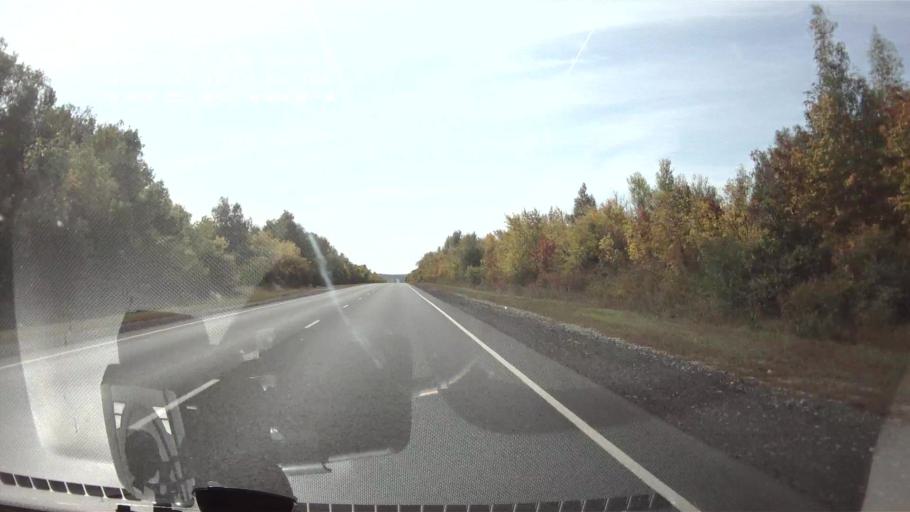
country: RU
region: Saratov
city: Khvalynsk
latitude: 52.6013
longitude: 48.1452
